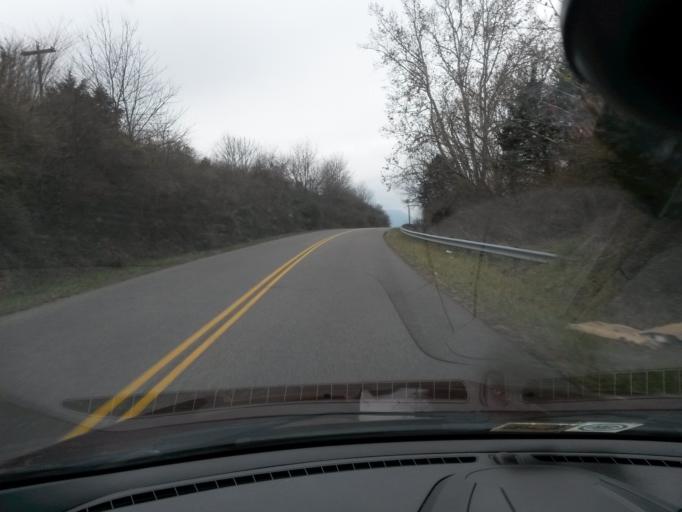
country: US
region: Virginia
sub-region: Rockbridge County
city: East Lexington
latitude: 37.7853
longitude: -79.3924
